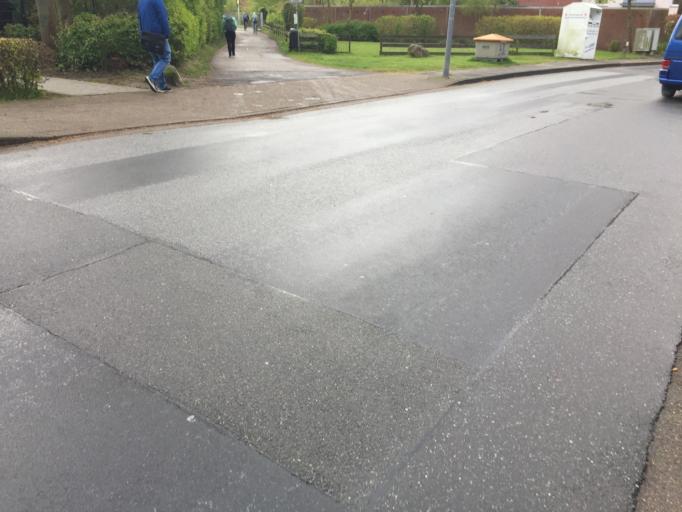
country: DE
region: Schleswig-Holstein
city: Flensburg
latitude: 54.7797
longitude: 9.4496
